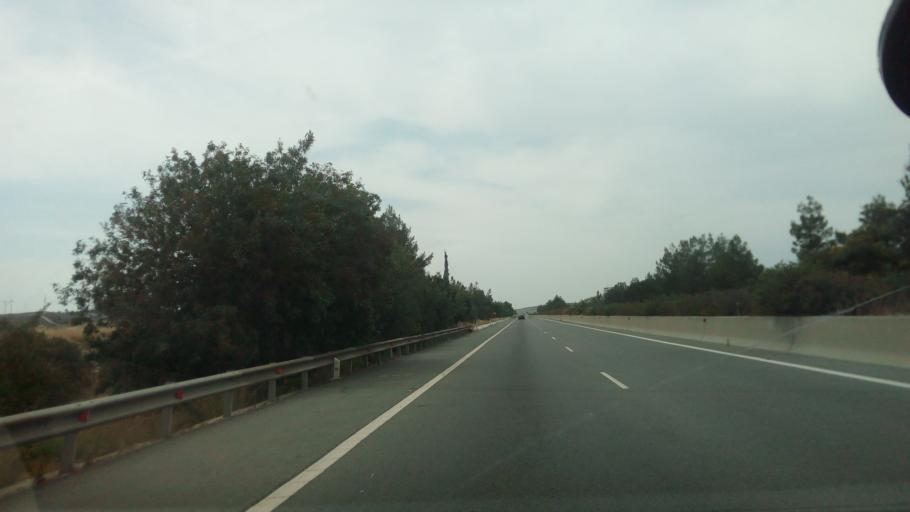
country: CY
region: Larnaka
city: Aradippou
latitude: 34.9658
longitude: 33.5588
